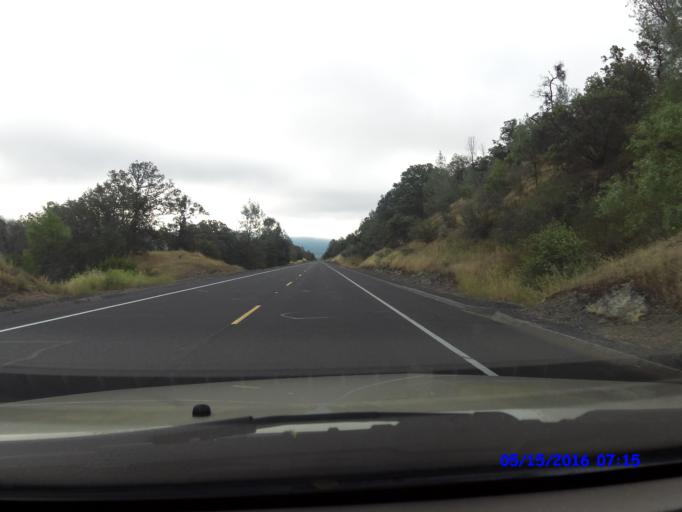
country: US
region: California
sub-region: Tuolumne County
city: Jamestown
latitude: 37.8256
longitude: -120.3373
